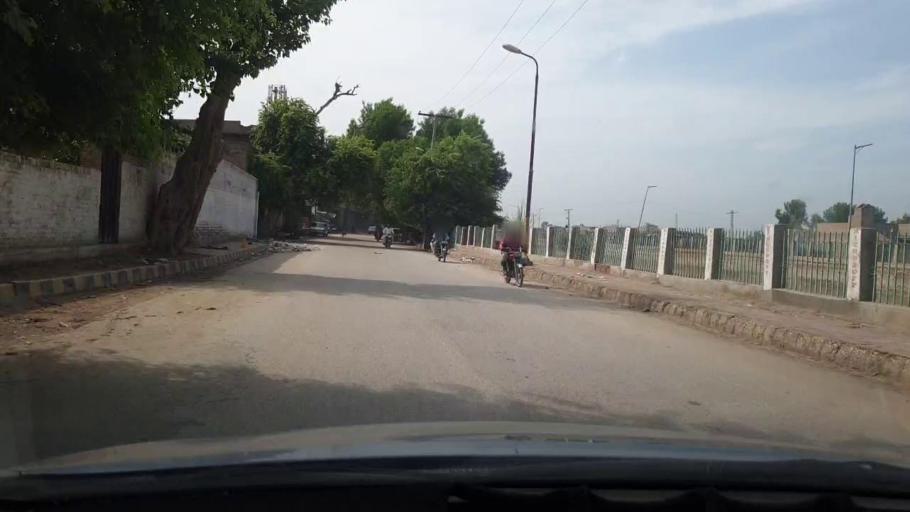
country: PK
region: Sindh
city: Khairpur
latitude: 27.5307
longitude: 68.7531
